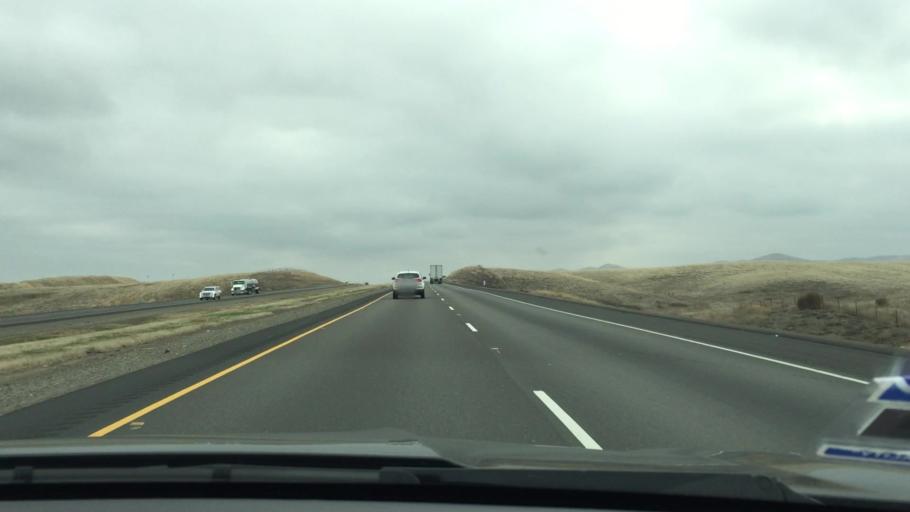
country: US
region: California
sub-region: Stanislaus County
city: Newman
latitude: 37.2698
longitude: -121.0951
